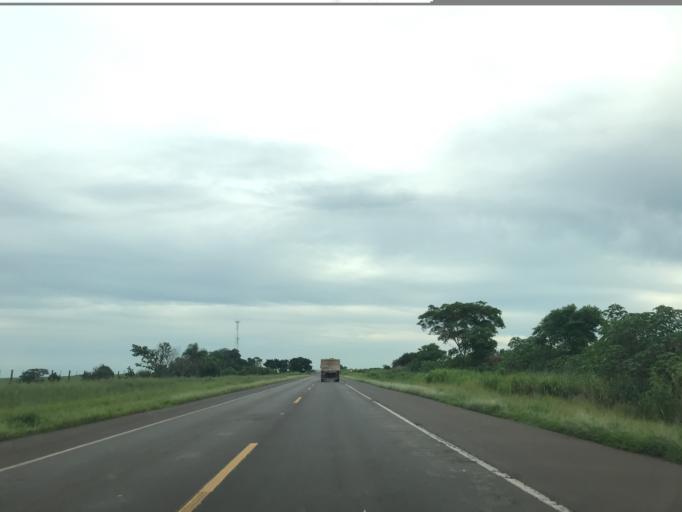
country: BR
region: Sao Paulo
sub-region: Tupa
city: Tupa
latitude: -21.6575
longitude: -50.5398
